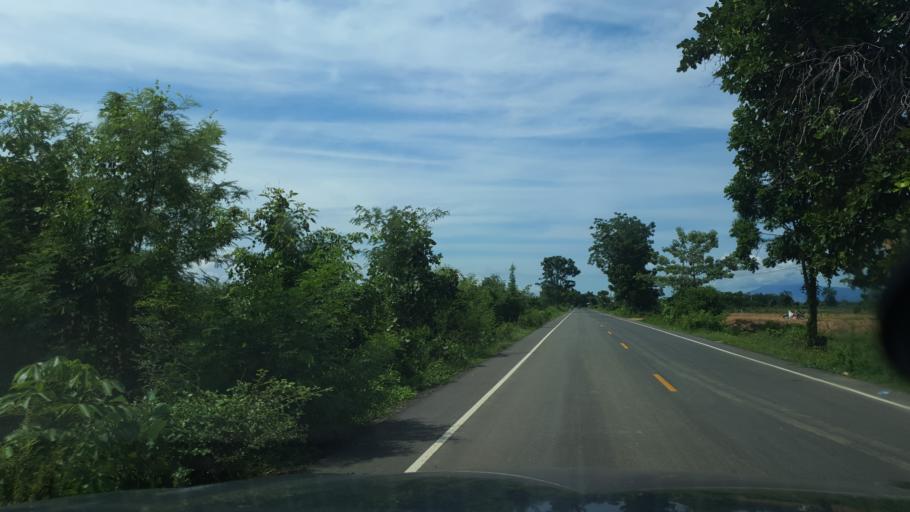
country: TH
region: Sukhothai
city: Si Samrong
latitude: 17.1795
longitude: 99.7372
